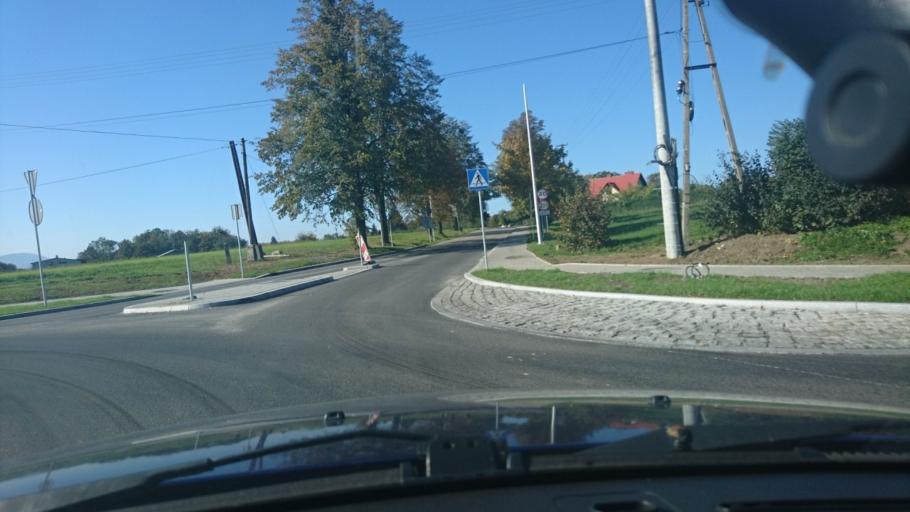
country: PL
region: Silesian Voivodeship
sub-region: Powiat bielski
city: Bronow
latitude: 49.8569
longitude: 18.8946
